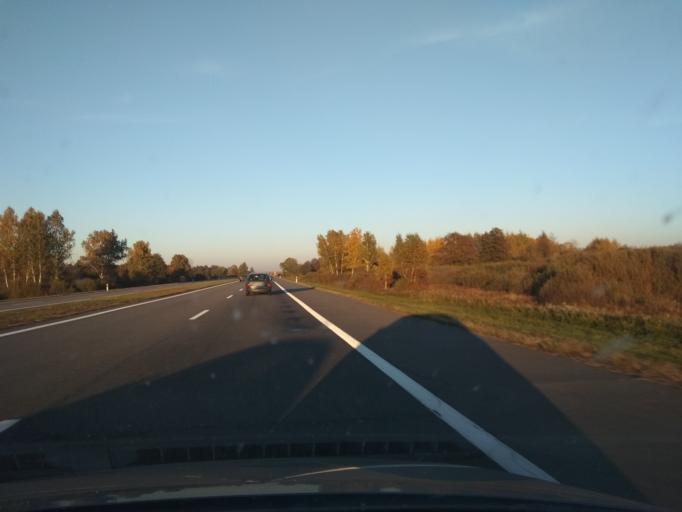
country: BY
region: Brest
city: Baranovichi
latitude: 53.2044
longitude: 26.1031
